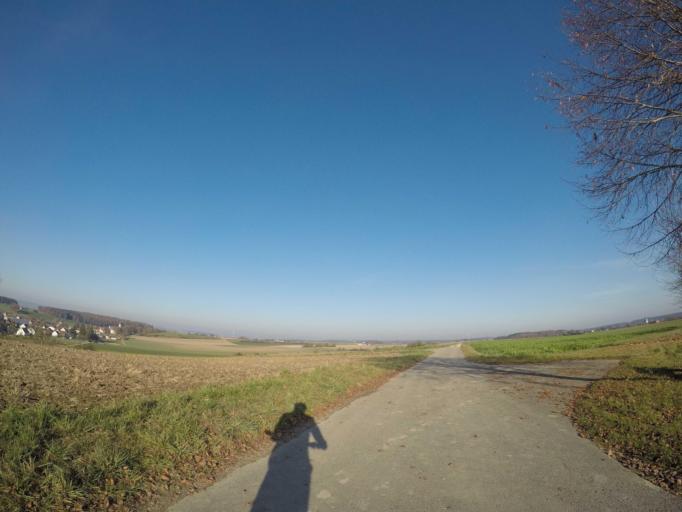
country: DE
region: Baden-Wuerttemberg
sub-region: Tuebingen Region
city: Grundsheim
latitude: 48.1699
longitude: 9.6685
